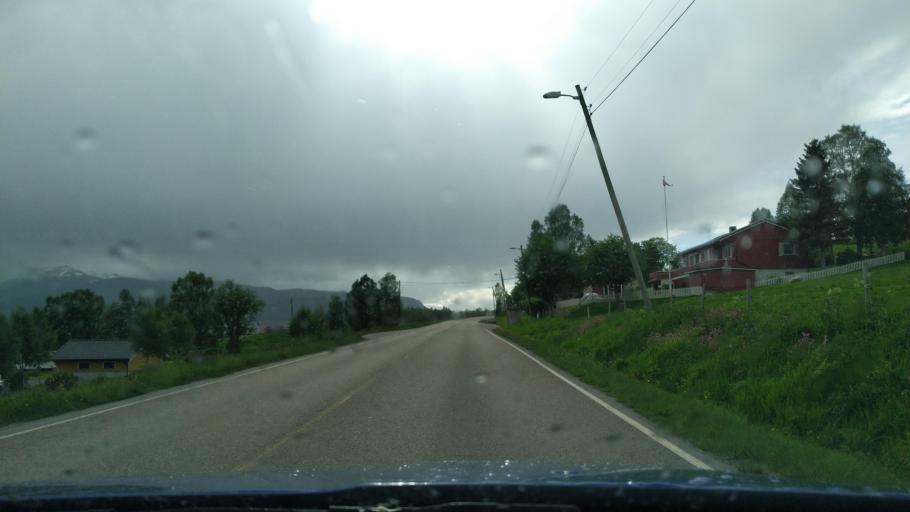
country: NO
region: Troms
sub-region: Sorreisa
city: Sorreisa
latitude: 69.1605
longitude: 18.1333
